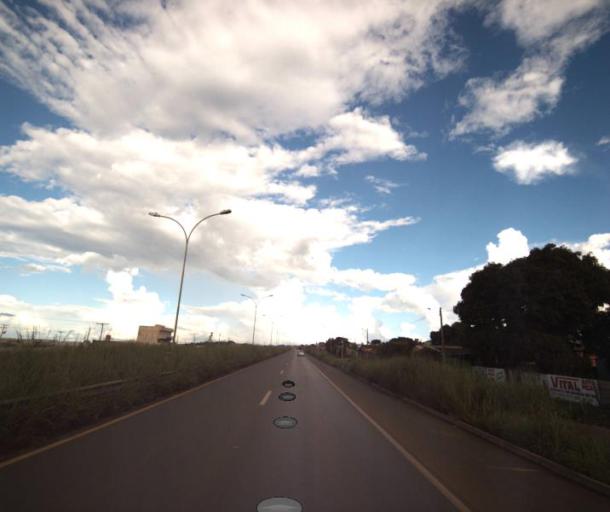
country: BR
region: Goias
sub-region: Anapolis
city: Anapolis
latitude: -16.2754
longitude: -48.9683
